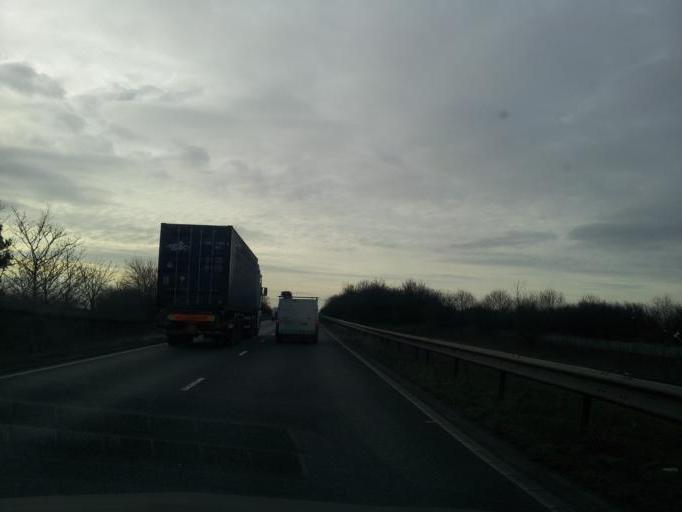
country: GB
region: England
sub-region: District of Rutland
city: Greetham
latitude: 52.7446
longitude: -0.6033
